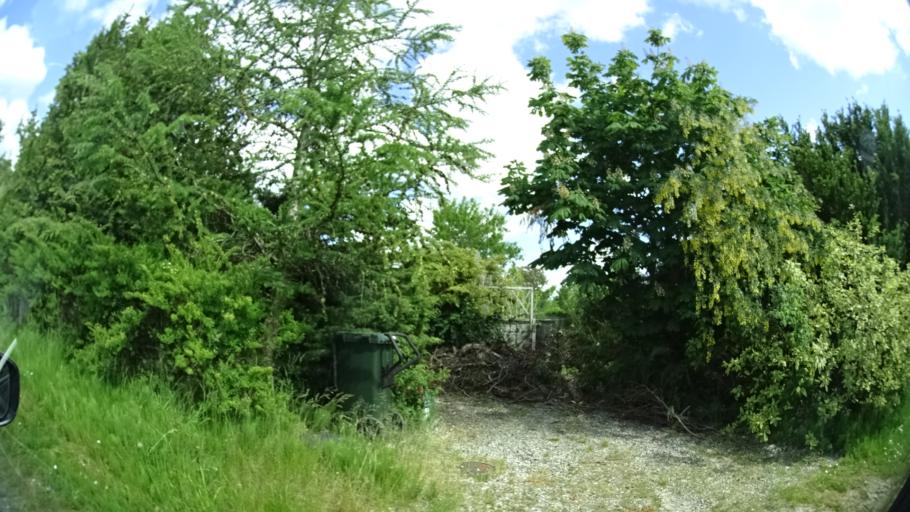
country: DK
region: Central Jutland
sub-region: Syddjurs Kommune
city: Ronde
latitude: 56.2964
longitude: 10.4197
